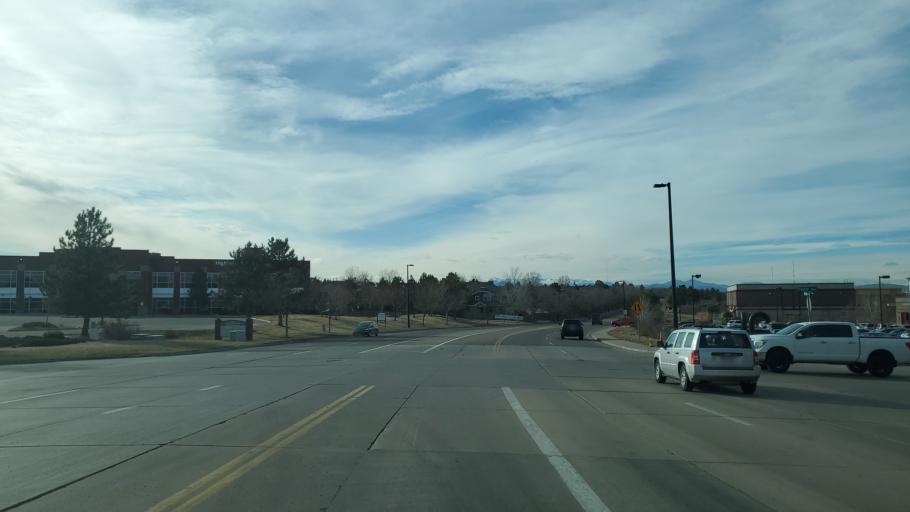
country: US
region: Colorado
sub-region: Douglas County
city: Acres Green
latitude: 39.5605
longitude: -104.9067
